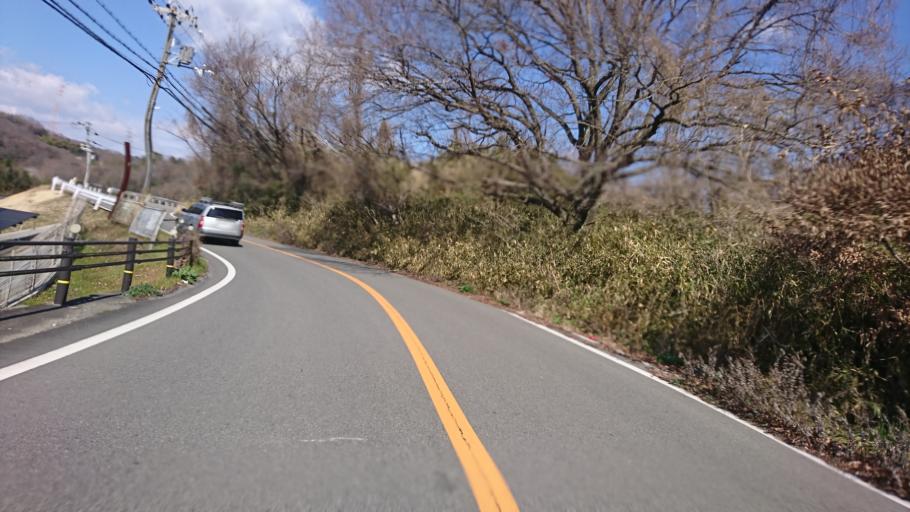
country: JP
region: Hyogo
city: Kakogawacho-honmachi
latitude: 34.8291
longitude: 134.8220
